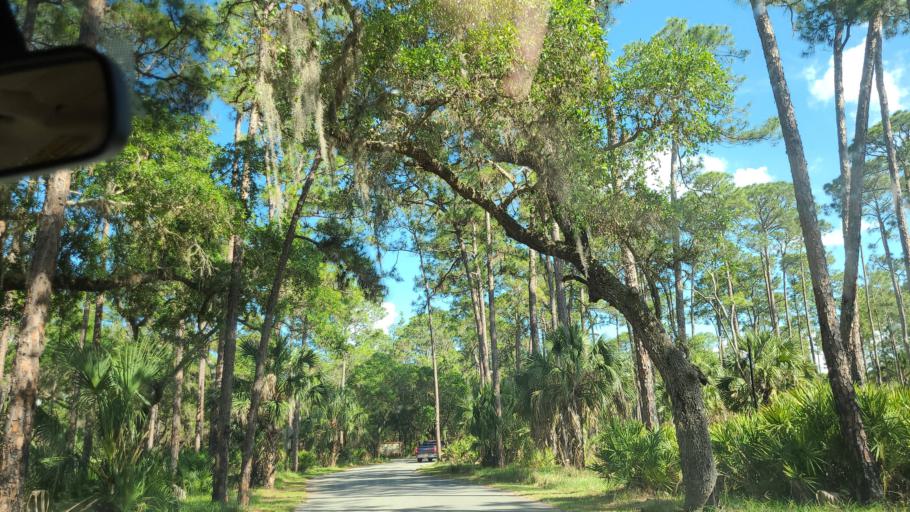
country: US
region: Florida
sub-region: Polk County
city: Babson Park
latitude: 27.9476
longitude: -81.3563
